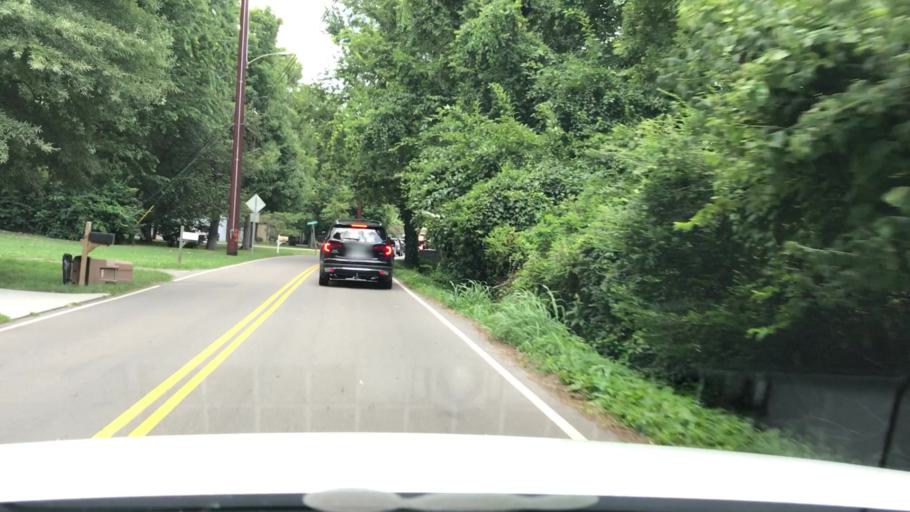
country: US
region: Tennessee
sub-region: Davidson County
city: Oak Hill
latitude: 36.1214
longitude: -86.8103
